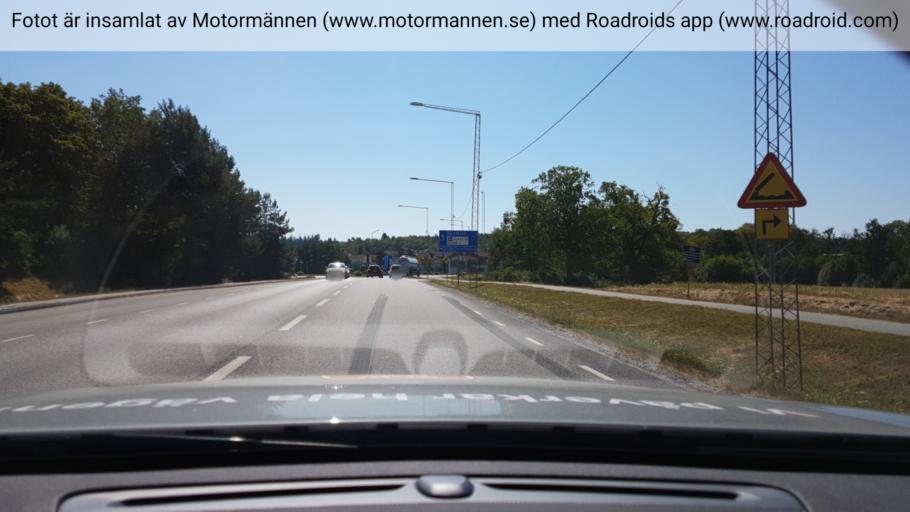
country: SE
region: Stockholm
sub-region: Ekero Kommun
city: Ekeroe
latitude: 59.2952
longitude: 17.8114
